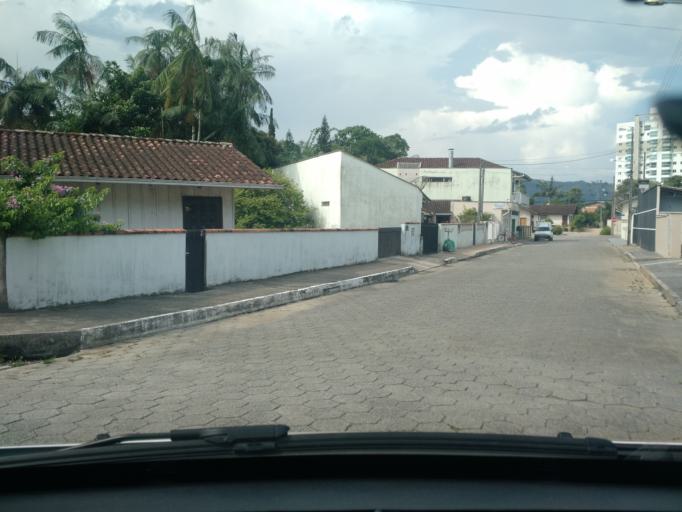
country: BR
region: Santa Catarina
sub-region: Jaragua Do Sul
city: Jaragua do Sul
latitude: -26.5073
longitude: -49.0884
